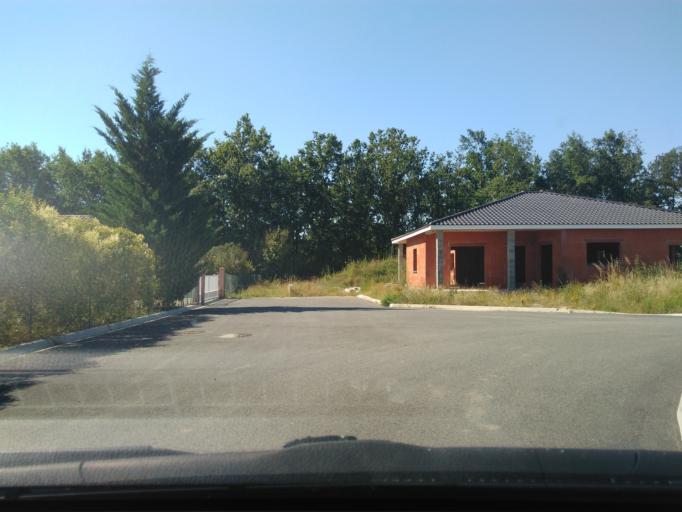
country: FR
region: Midi-Pyrenees
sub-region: Departement du Tarn-et-Garonne
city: Montauban
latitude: 44.0559
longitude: 1.3379
